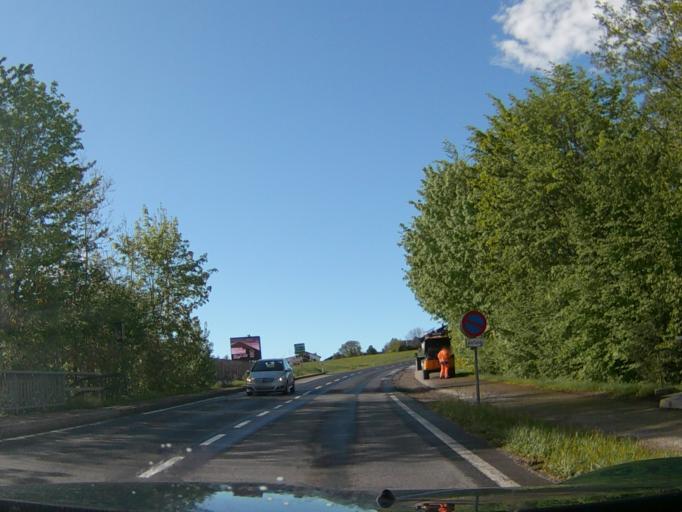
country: AT
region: Upper Austria
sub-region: Politischer Bezirk Vocklabruck
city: Mondsee
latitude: 47.8539
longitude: 13.3435
